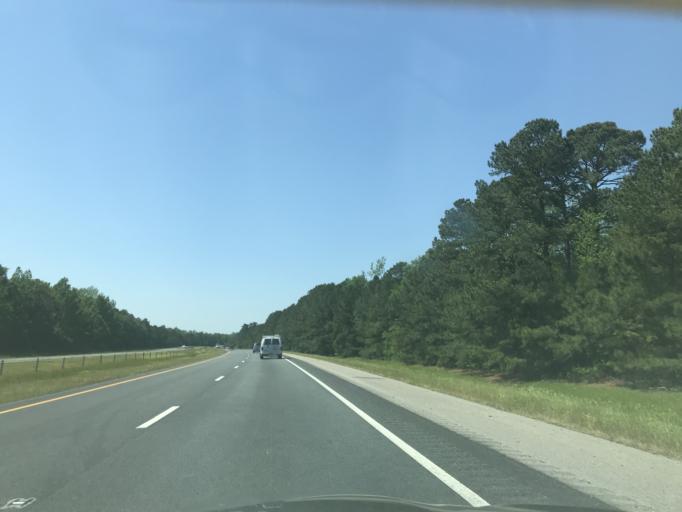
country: US
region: North Carolina
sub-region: Johnston County
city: Benson
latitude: 35.3417
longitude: -78.4668
